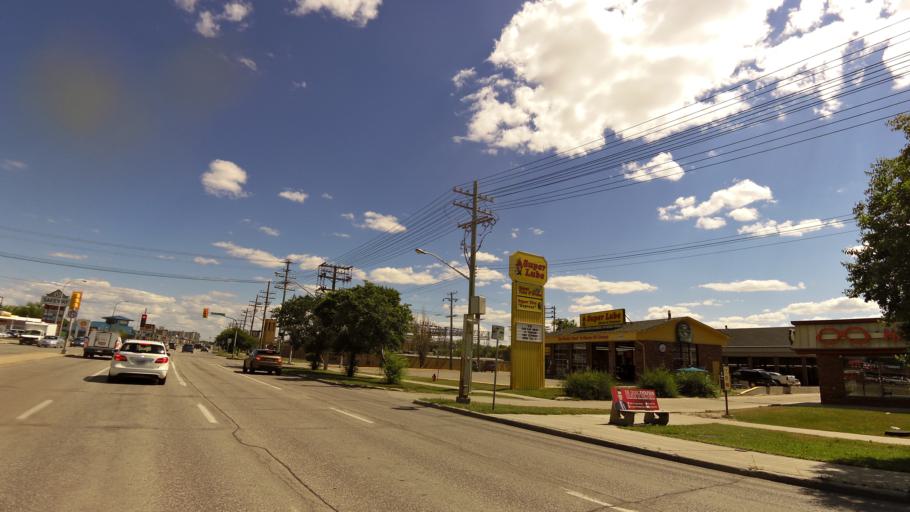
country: CA
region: Manitoba
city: Headingley
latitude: 49.8829
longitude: -97.3014
